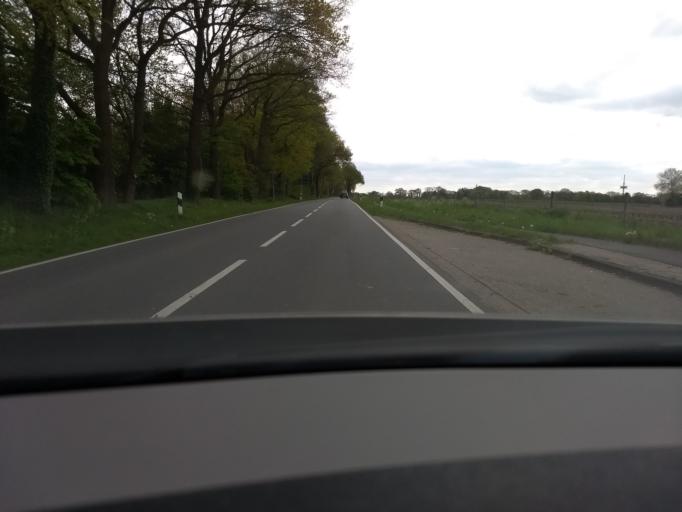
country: DE
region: Lower Saxony
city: Rastede
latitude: 53.2258
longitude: 8.2560
